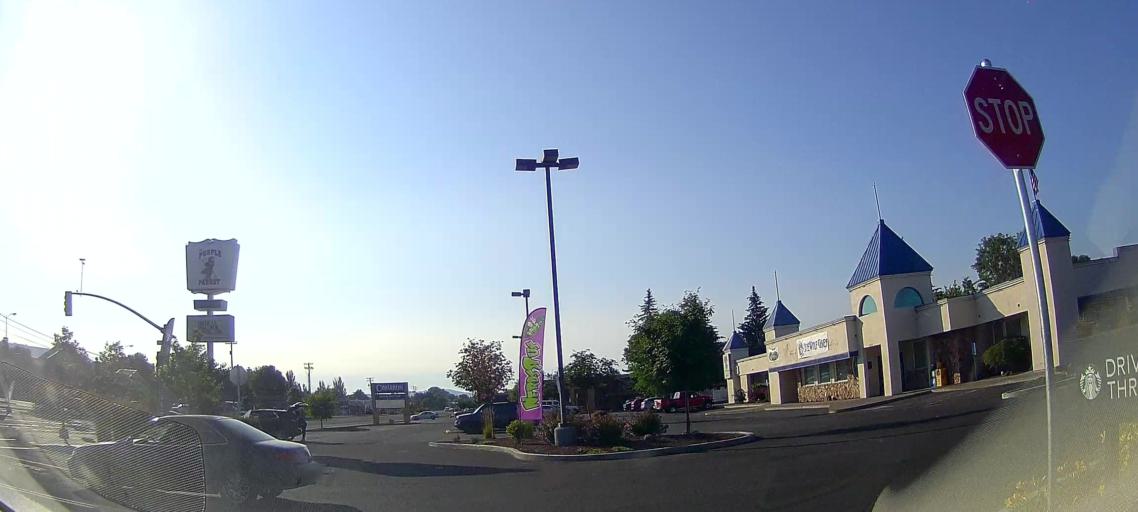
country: US
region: Oregon
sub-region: Klamath County
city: Altamont
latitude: 42.2086
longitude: -121.7525
